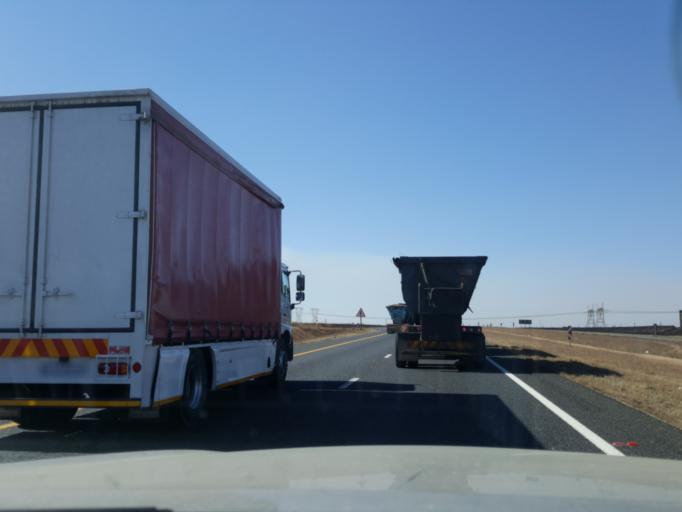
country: ZA
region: Mpumalanga
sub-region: Nkangala District Municipality
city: Delmas
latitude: -26.0234
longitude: 28.8857
